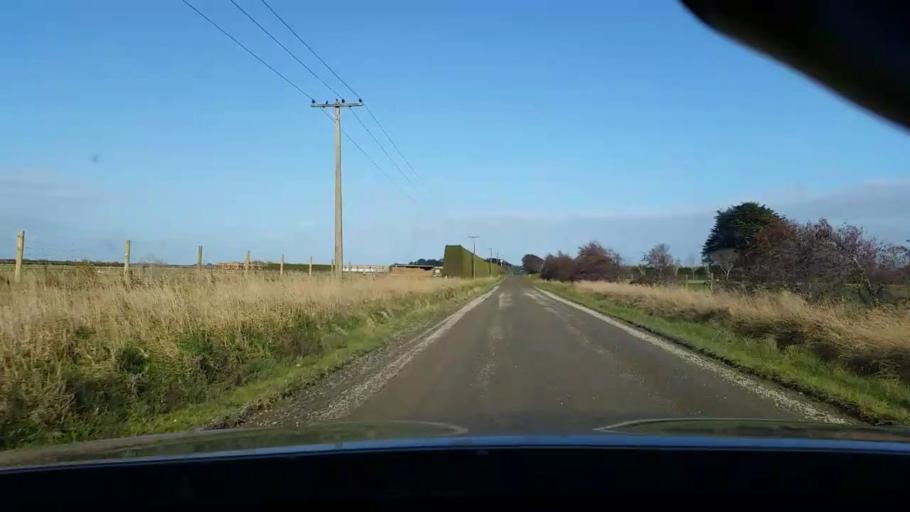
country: NZ
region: Southland
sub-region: Invercargill City
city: Invercargill
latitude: -46.3000
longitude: 168.3033
